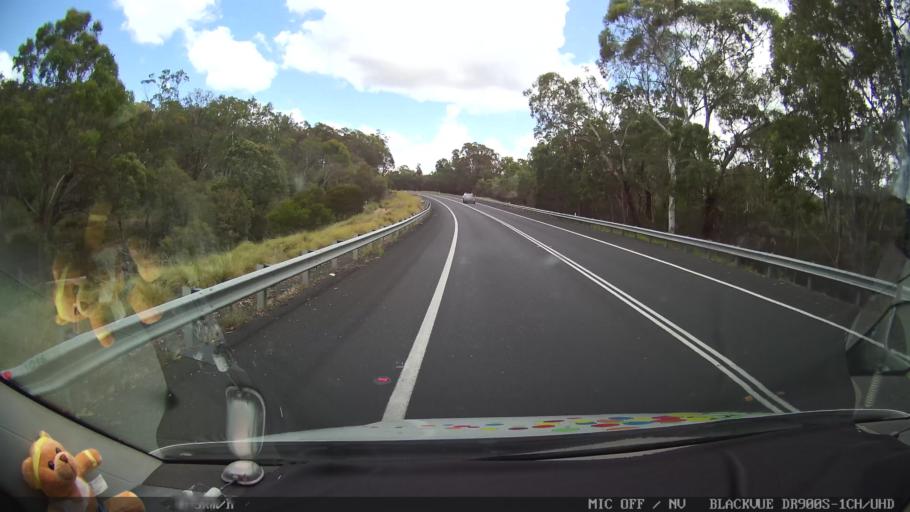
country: AU
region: New South Wales
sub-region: Glen Innes Severn
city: Glen Innes
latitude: -29.3534
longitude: 151.8975
